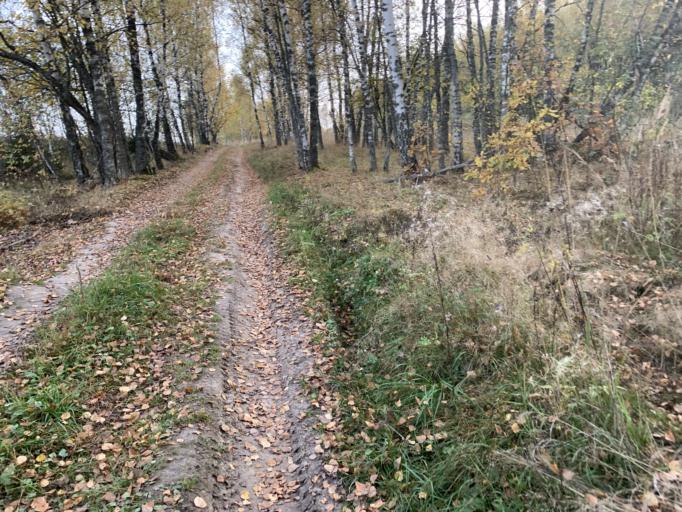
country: RU
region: Jaroslavl
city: Porech'ye-Rybnoye
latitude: 56.9852
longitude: 39.3803
